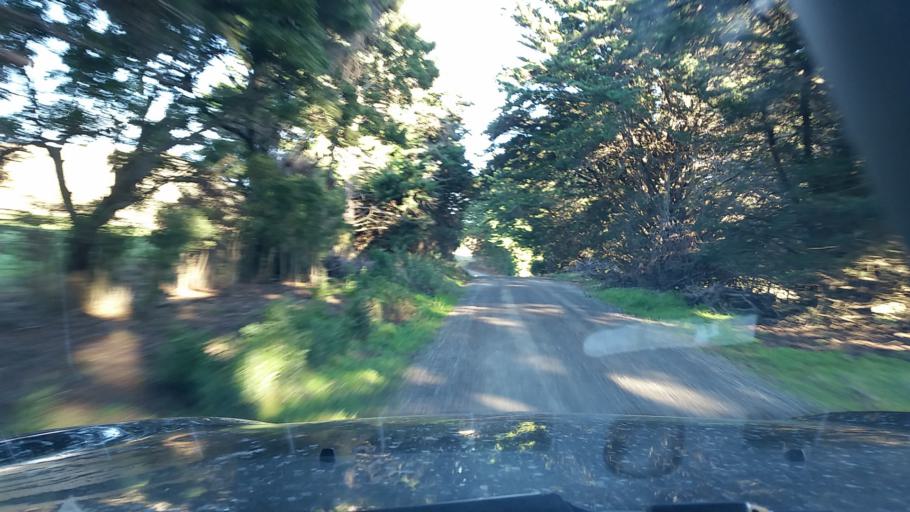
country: NZ
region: Marlborough
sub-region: Marlborough District
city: Blenheim
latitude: -41.7352
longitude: 173.9985
